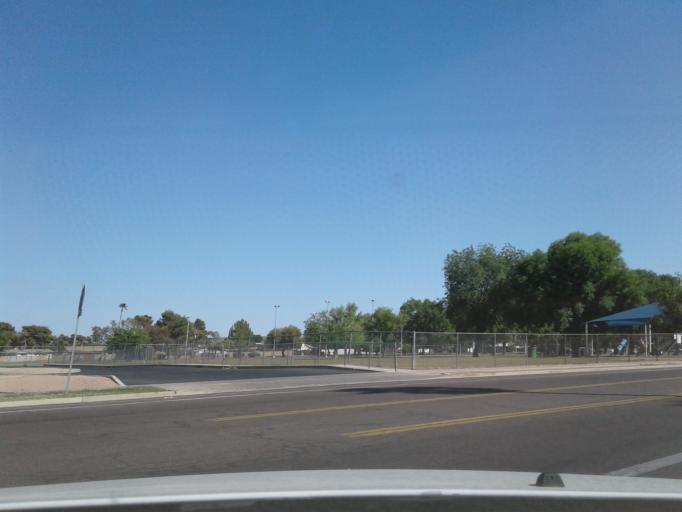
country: US
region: Arizona
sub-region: Maricopa County
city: Tempe
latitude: 33.4010
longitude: -111.9155
